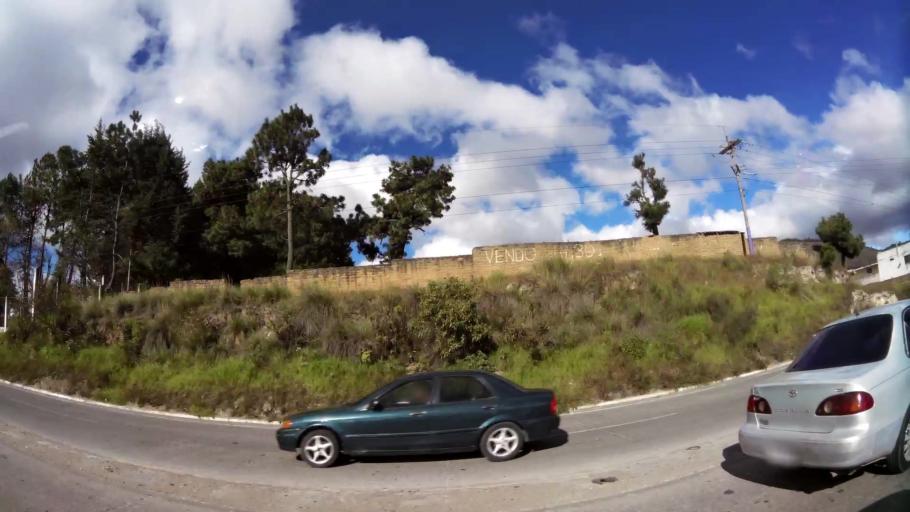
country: GT
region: Quetzaltenango
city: Salcaja
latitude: 14.8956
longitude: -91.4540
